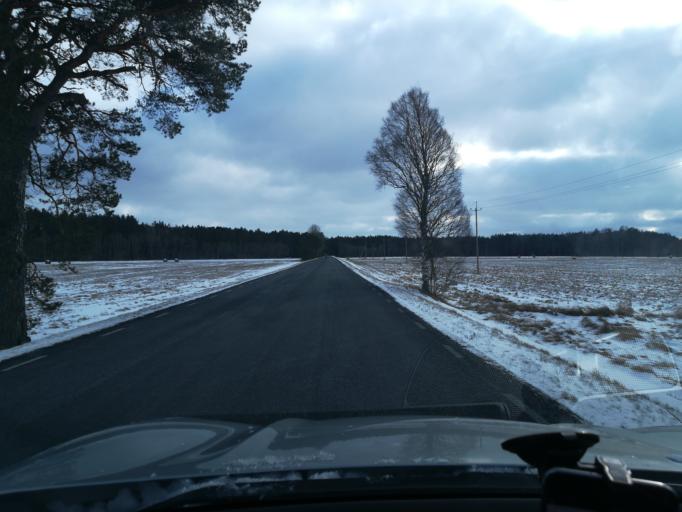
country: EE
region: Harju
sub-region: Keila linn
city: Keila
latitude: 59.4099
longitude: 24.4106
